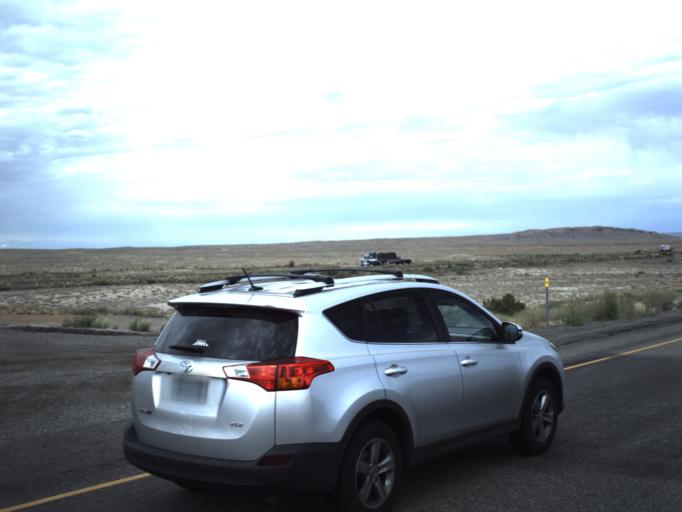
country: US
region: Utah
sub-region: Grand County
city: Moab
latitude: 38.9395
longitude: -109.5087
